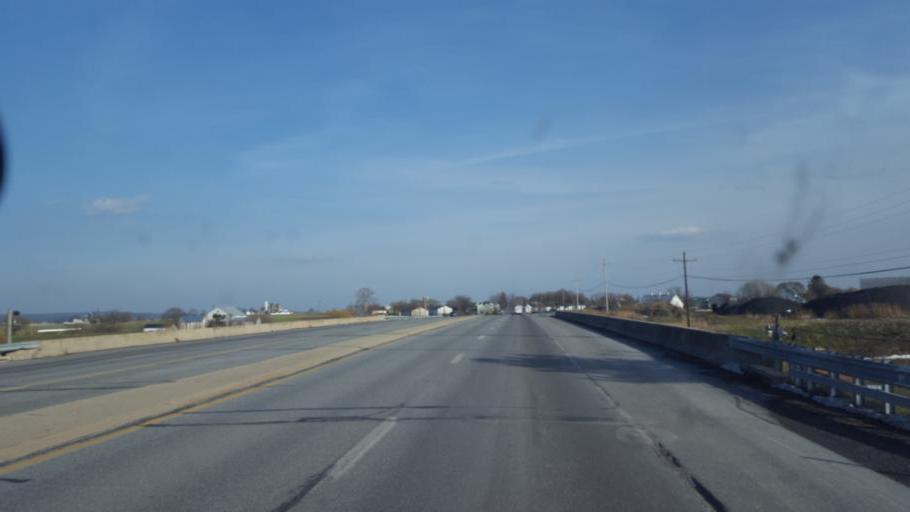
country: US
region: Pennsylvania
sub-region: Lancaster County
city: Brownstown
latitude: 40.0753
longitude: -76.1803
